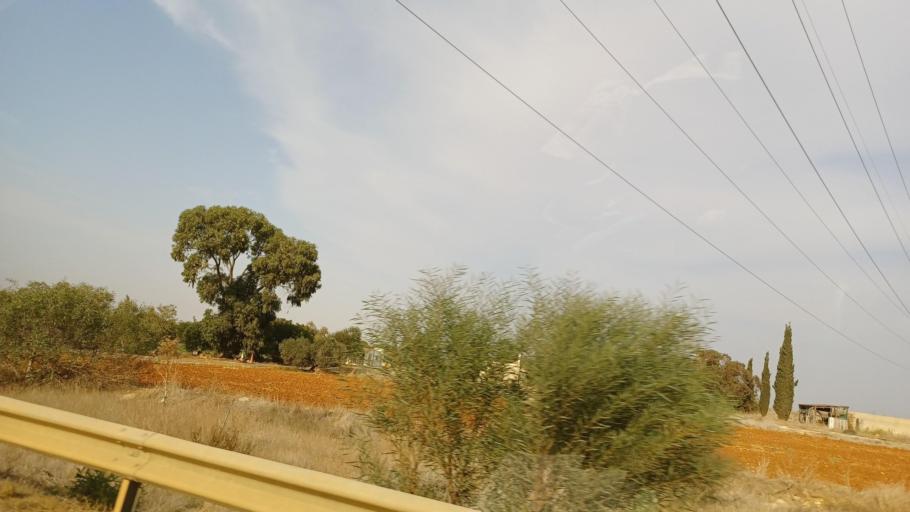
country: CY
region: Ammochostos
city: Frenaros
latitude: 35.0607
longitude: 33.8958
